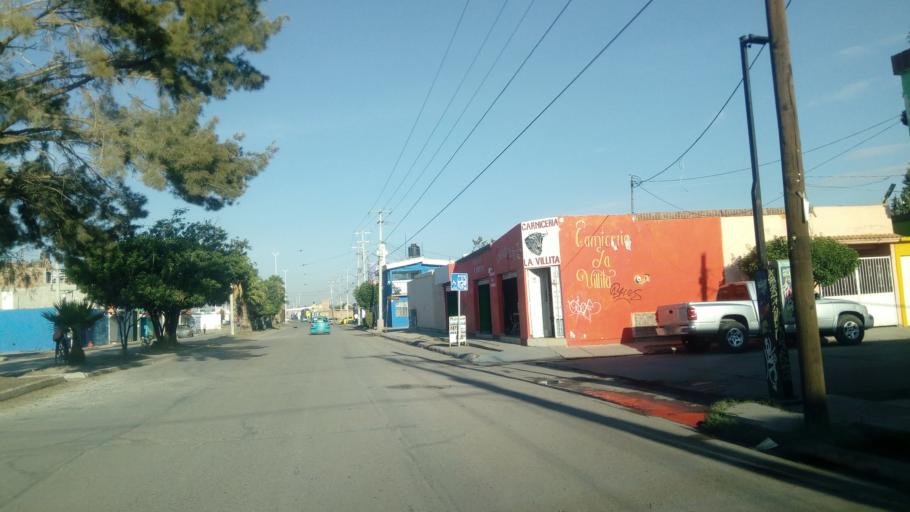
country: MX
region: Durango
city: Victoria de Durango
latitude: 24.0574
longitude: -104.5854
